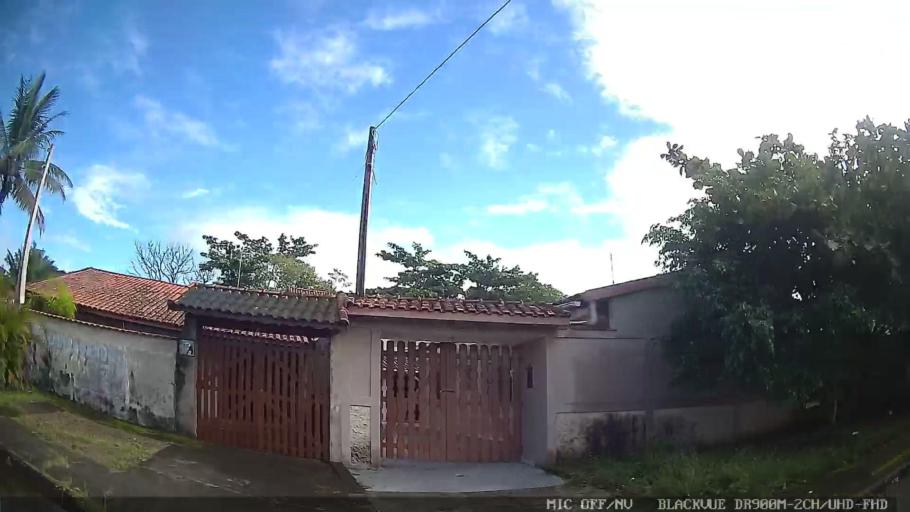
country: BR
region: Sao Paulo
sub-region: Itanhaem
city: Itanhaem
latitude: -24.2389
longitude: -46.8885
